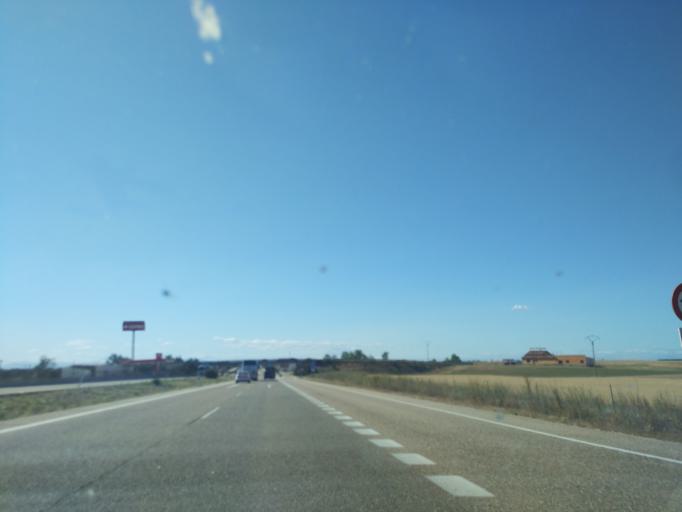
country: ES
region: Castille and Leon
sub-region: Provincia de Zamora
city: San Esteban del Molar
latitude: 41.9356
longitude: -5.5425
